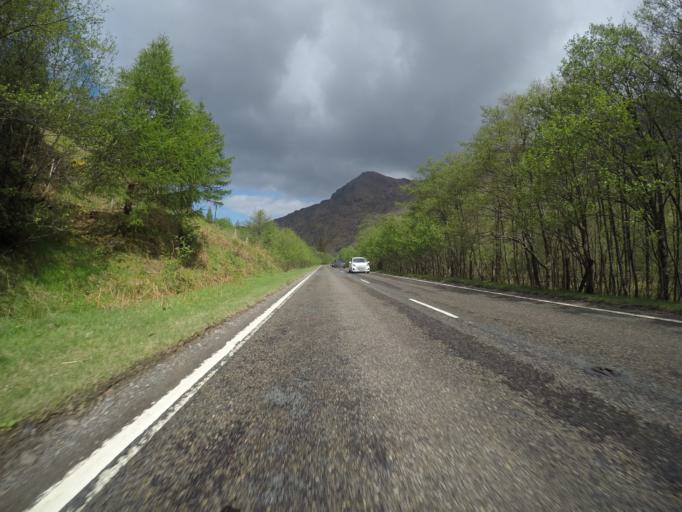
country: GB
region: Scotland
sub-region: Highland
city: Fort William
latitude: 57.2003
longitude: -5.3933
